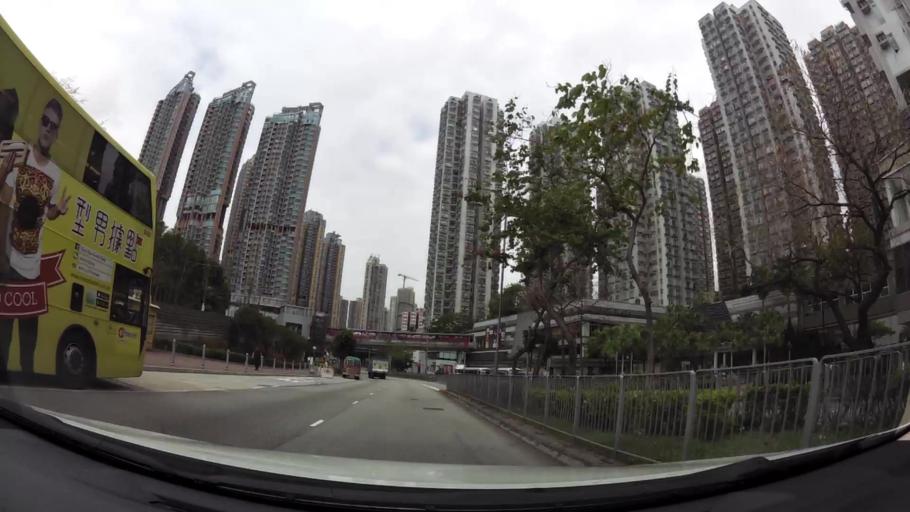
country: HK
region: Tuen Mun
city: Tuen Mun
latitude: 22.3924
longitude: 113.9752
